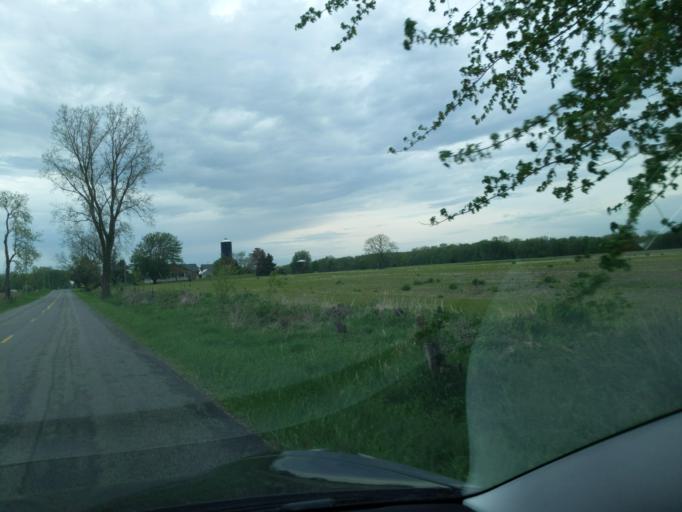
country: US
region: Michigan
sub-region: Ingham County
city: Stockbridge
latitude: 42.4356
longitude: -84.2583
